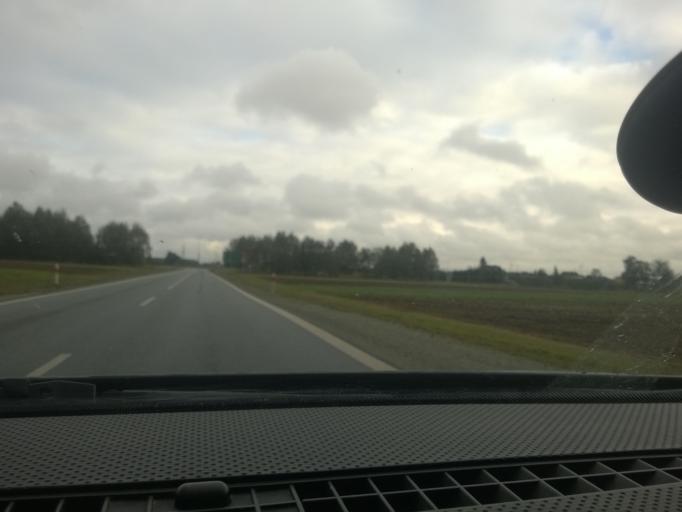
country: PL
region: Lodz Voivodeship
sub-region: Powiat sieradzki
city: Wroblew
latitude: 51.5820
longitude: 18.6691
